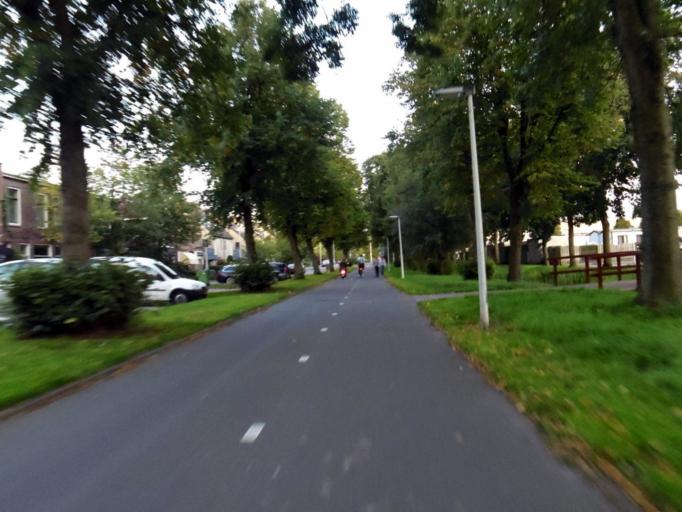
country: NL
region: South Holland
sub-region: Gemeente Voorschoten
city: Voorschoten
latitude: 52.1529
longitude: 4.4581
